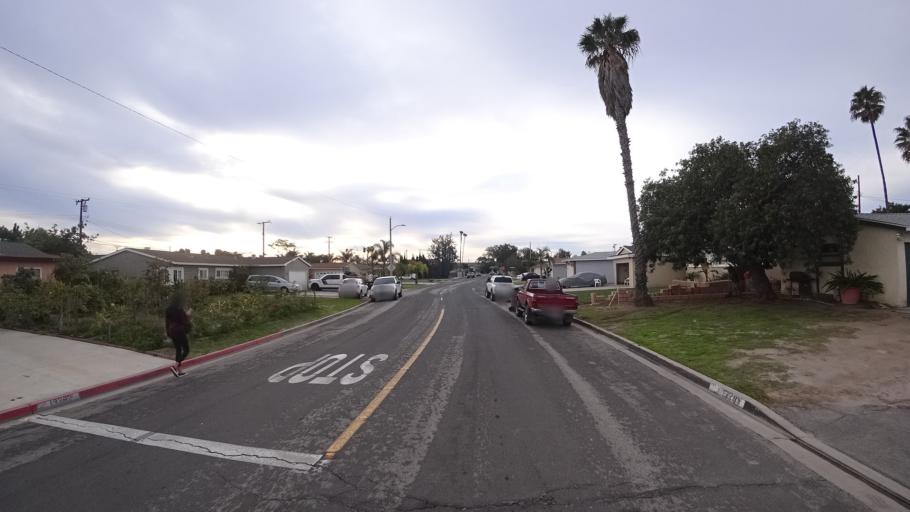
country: US
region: California
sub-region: Orange County
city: Garden Grove
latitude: 33.7701
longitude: -117.9244
